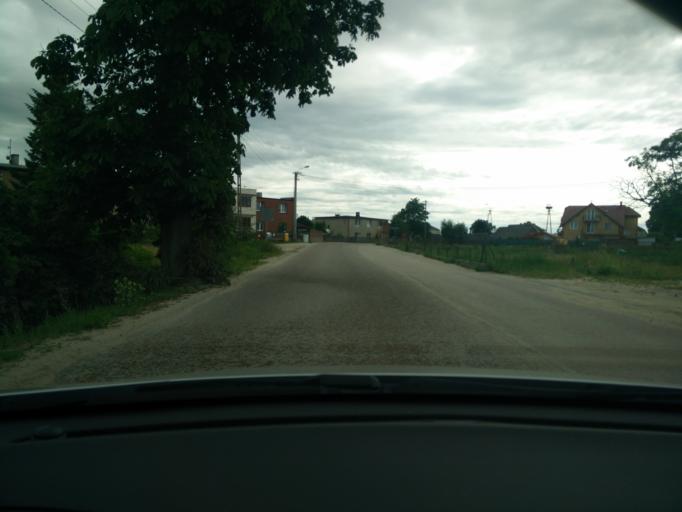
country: PL
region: Pomeranian Voivodeship
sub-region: Powiat pucki
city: Mrzezino
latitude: 54.6531
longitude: 18.4318
